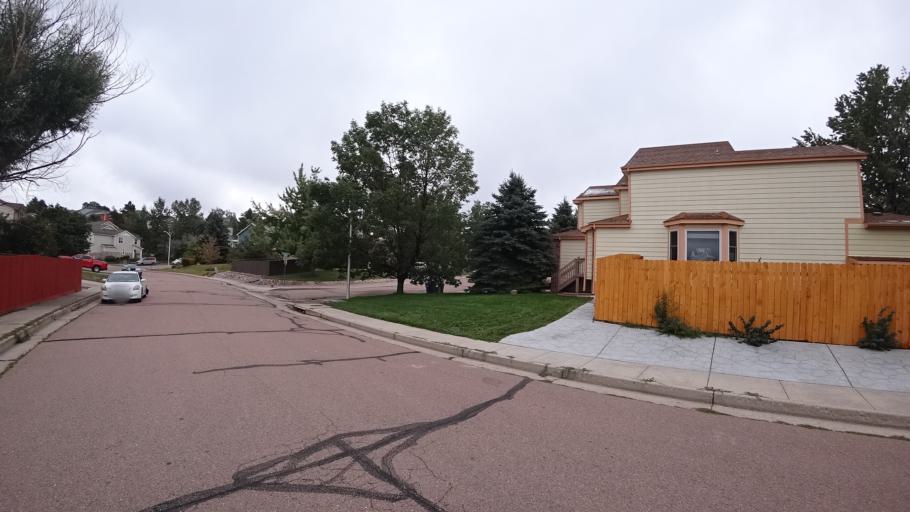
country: US
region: Colorado
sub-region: El Paso County
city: Cimarron Hills
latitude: 38.9247
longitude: -104.7565
